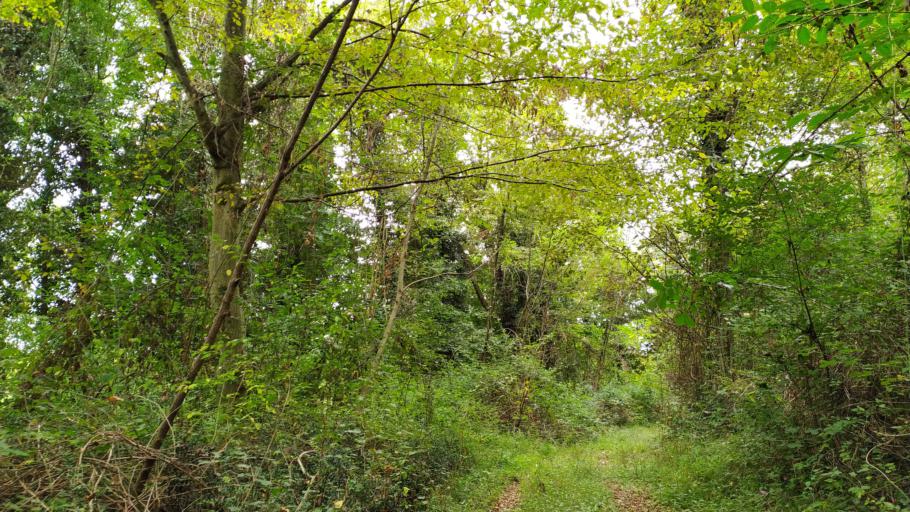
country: IT
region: Friuli Venezia Giulia
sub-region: Provincia di Pordenone
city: Aviano-Castello
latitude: 46.0750
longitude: 12.5759
